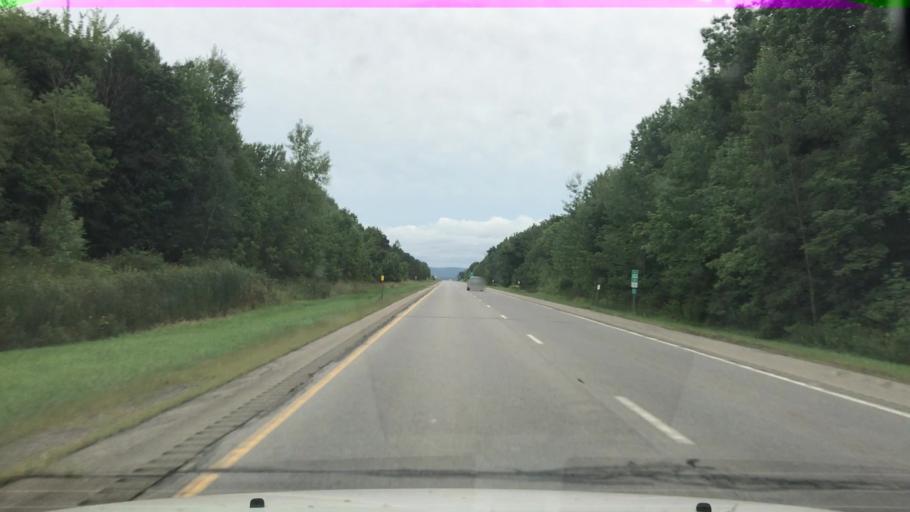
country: US
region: New York
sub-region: Erie County
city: Springville
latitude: 42.5331
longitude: -78.7051
